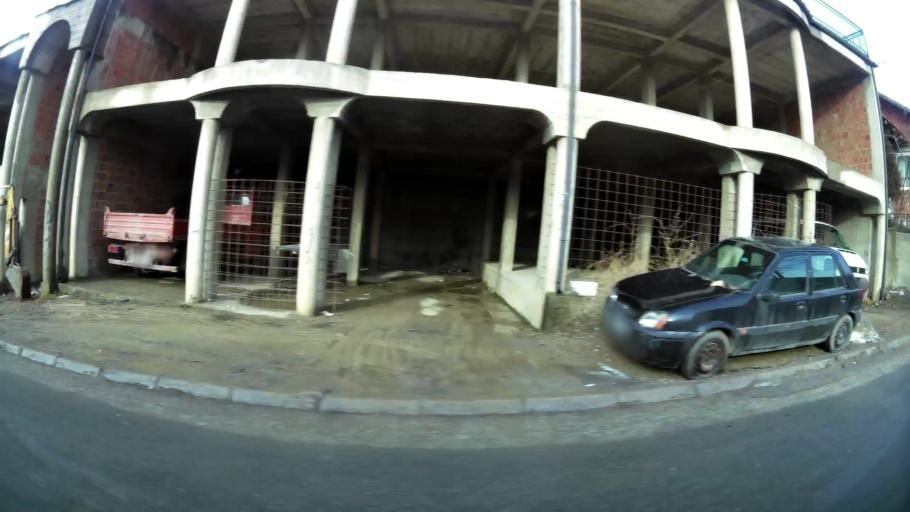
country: XK
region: Pristina
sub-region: Komuna e Prishtines
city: Pristina
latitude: 42.6707
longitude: 21.1855
